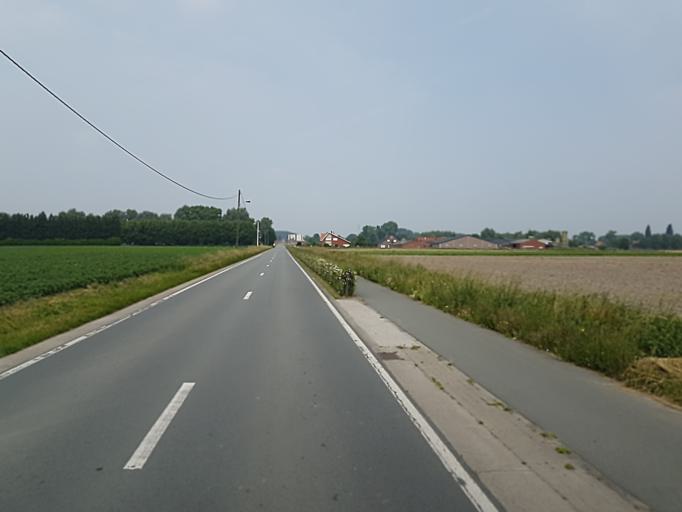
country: BE
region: Flanders
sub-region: Provincie West-Vlaanderen
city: Ardooie
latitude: 50.9505
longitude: 3.2007
